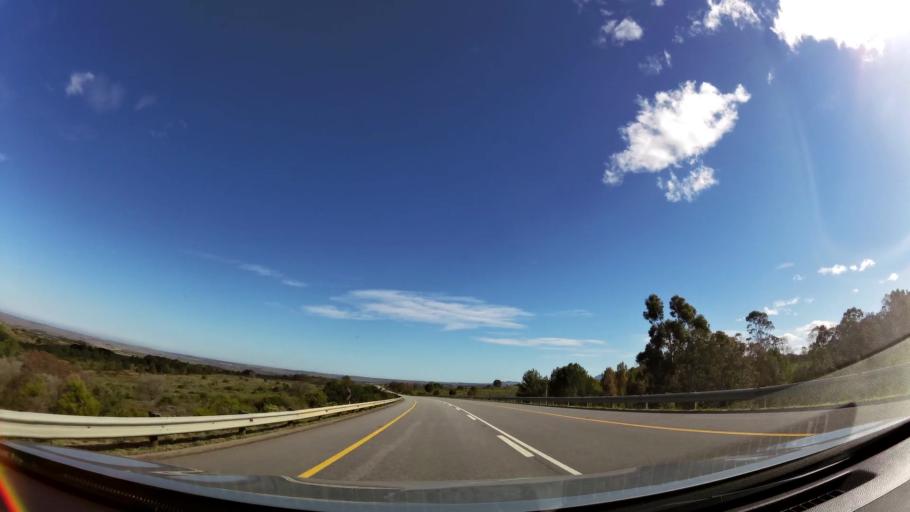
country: ZA
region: Eastern Cape
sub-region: Cacadu District Municipality
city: Kruisfontein
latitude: -33.9951
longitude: 24.6921
